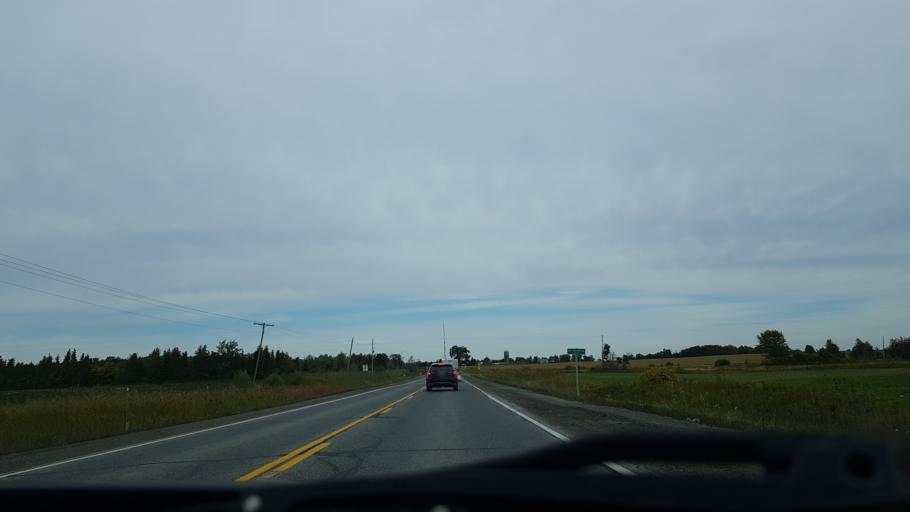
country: CA
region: Ontario
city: Orangeville
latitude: 43.8973
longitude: -79.9540
